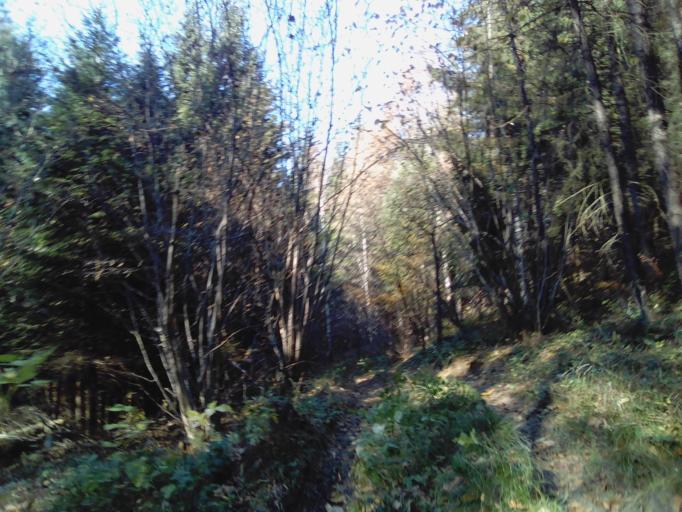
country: PL
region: Subcarpathian Voivodeship
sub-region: Powiat strzyzowski
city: Wisniowa
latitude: 49.8493
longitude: 21.6615
